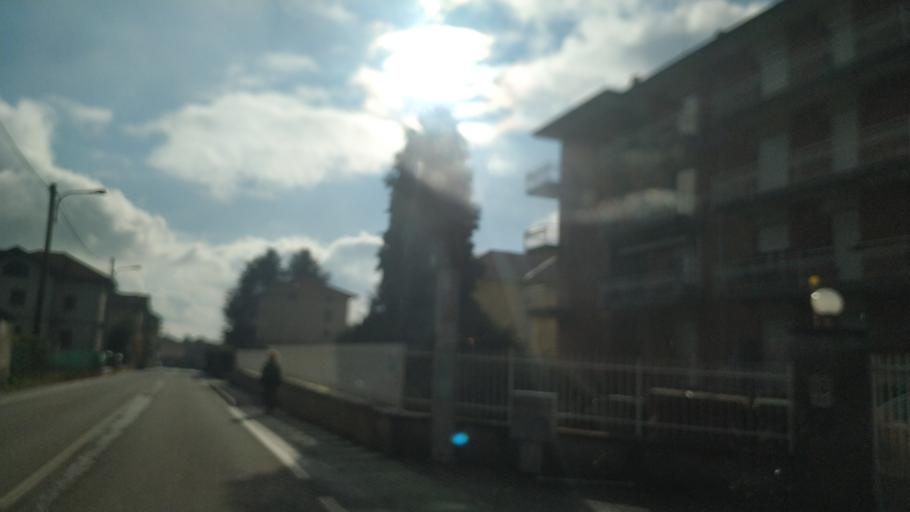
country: IT
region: Piedmont
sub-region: Provincia di Biella
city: Ponderano
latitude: 45.5407
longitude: 8.0537
